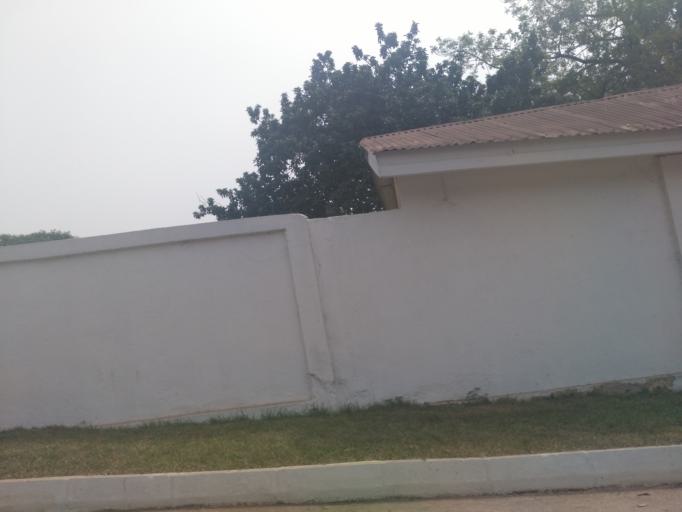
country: GH
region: Ashanti
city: Kumasi
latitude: 6.6825
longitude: -1.6327
